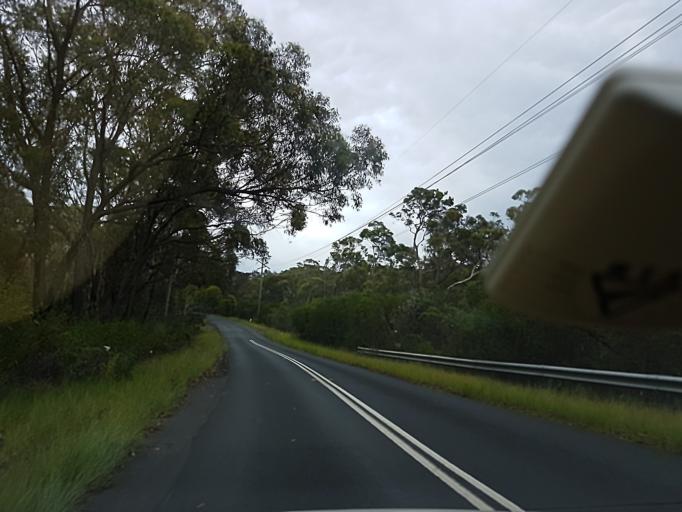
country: AU
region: New South Wales
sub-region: Warringah
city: Davidson
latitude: -33.7262
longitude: 151.2314
